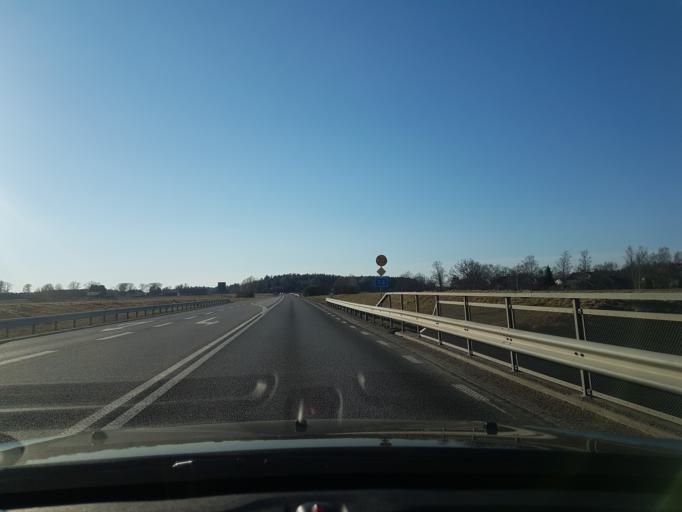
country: SE
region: Uppsala
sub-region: Enkopings Kommun
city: Orsundsbro
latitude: 59.8562
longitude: 17.4282
